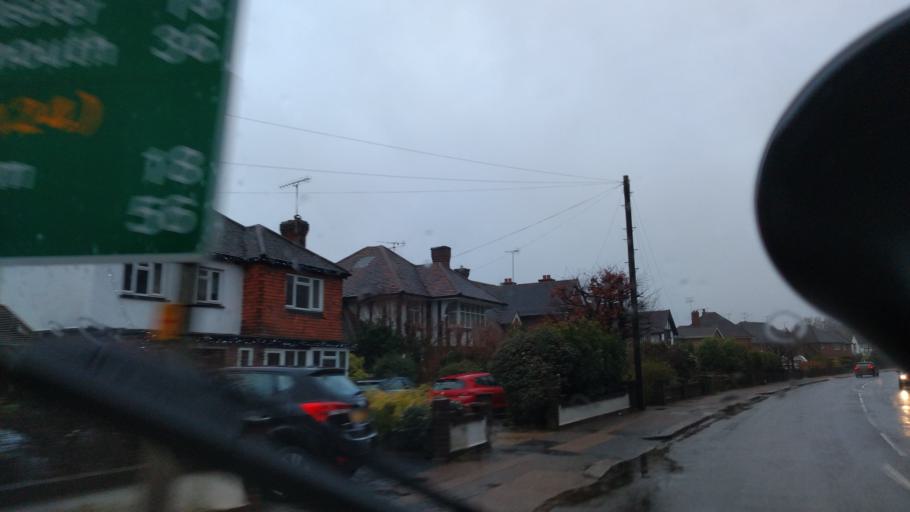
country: GB
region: England
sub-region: West Sussex
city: Broadwater
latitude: 50.8340
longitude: -0.3834
